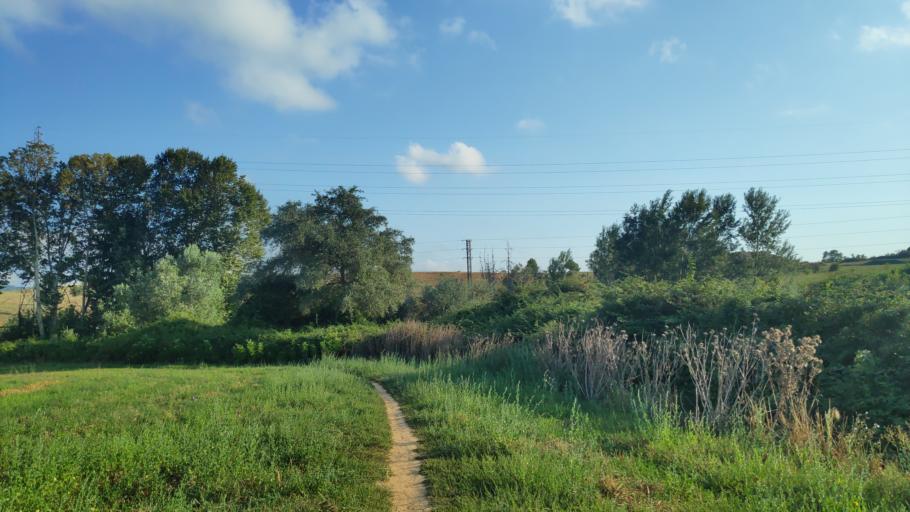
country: ES
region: Catalonia
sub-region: Provincia de Barcelona
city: Cerdanyola del Valles
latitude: 41.4940
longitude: 2.1205
